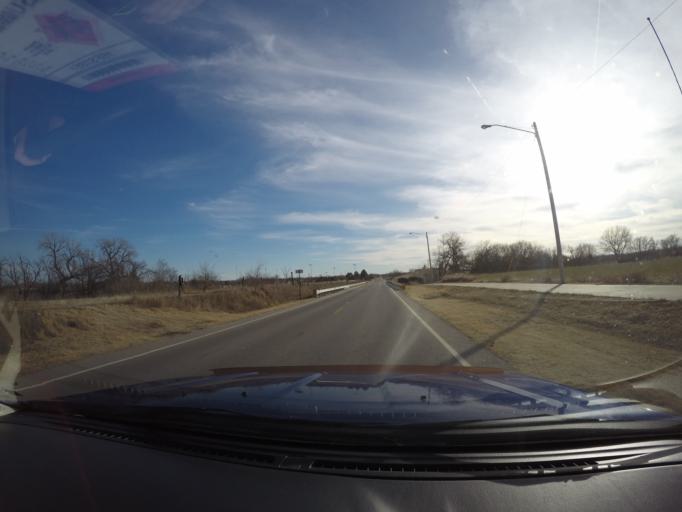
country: US
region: Kansas
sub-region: Harvey County
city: North Newton
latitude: 38.0671
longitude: -97.3367
